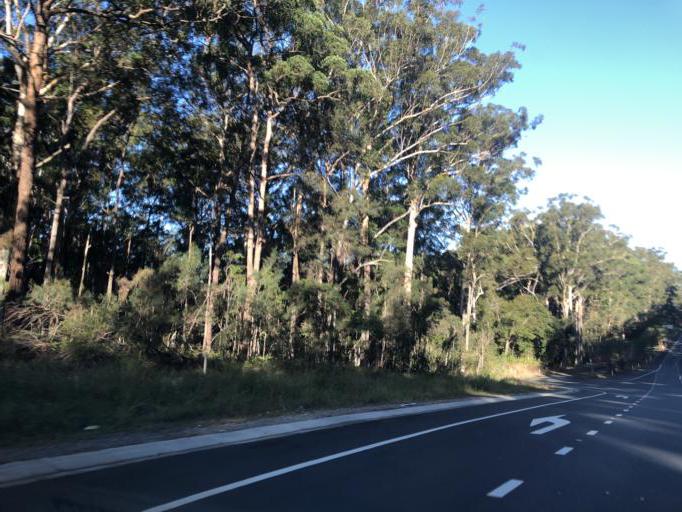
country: AU
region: New South Wales
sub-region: Nambucca Shire
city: Nambucca
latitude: -30.5466
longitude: 153.0073
